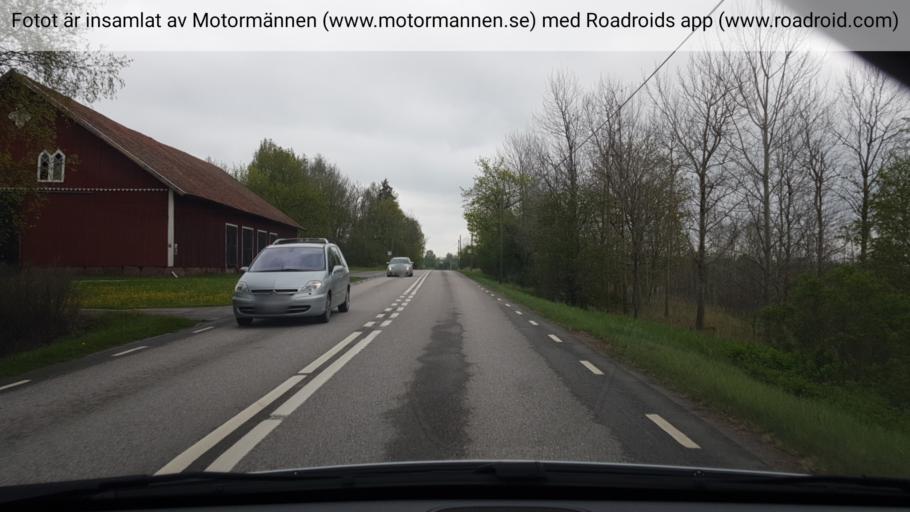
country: SE
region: Vaestra Goetaland
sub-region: Skovde Kommun
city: Stopen
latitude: 58.5199
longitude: 13.9790
